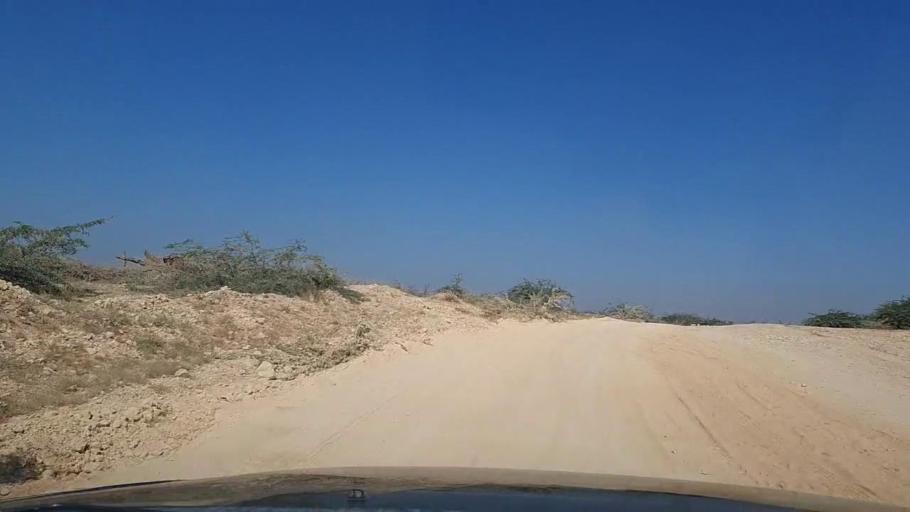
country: PK
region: Sindh
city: Thatta
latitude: 24.6208
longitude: 67.8395
